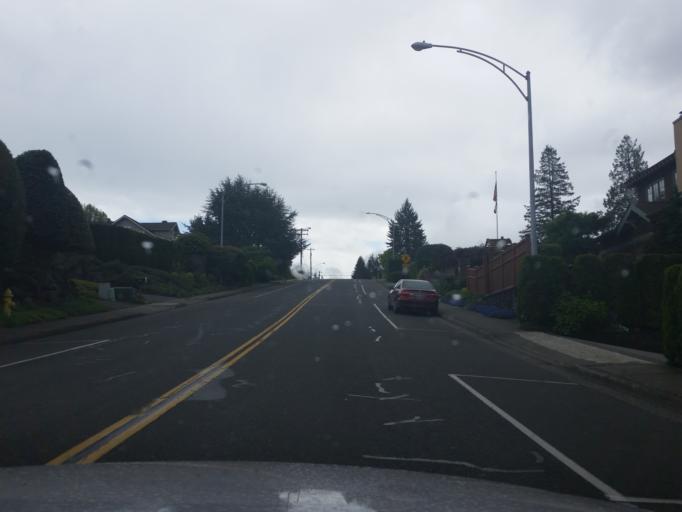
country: US
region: Washington
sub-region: Snohomish County
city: Edmonds
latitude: 47.8154
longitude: -122.3670
